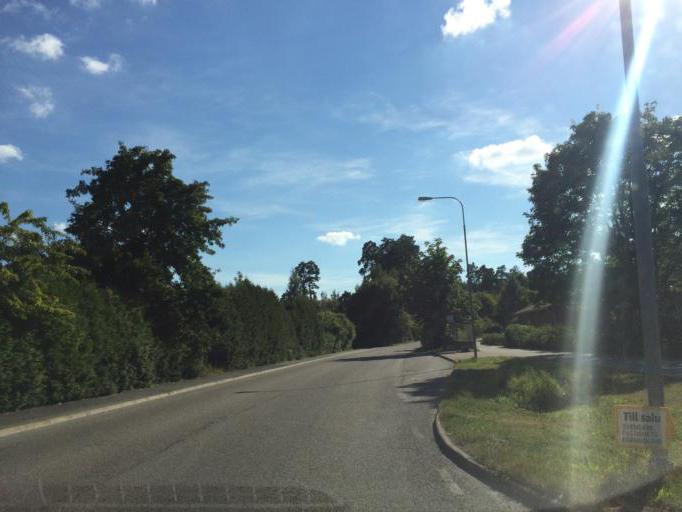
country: SE
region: Stockholm
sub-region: Upplands Vasby Kommun
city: Upplands Vaesby
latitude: 59.4902
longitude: 17.9464
